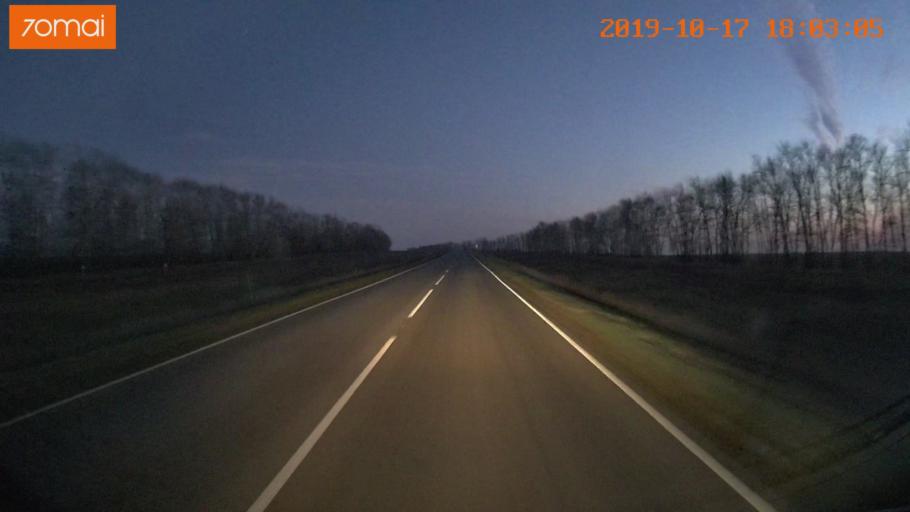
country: RU
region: Tula
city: Kurkino
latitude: 53.4991
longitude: 38.6208
